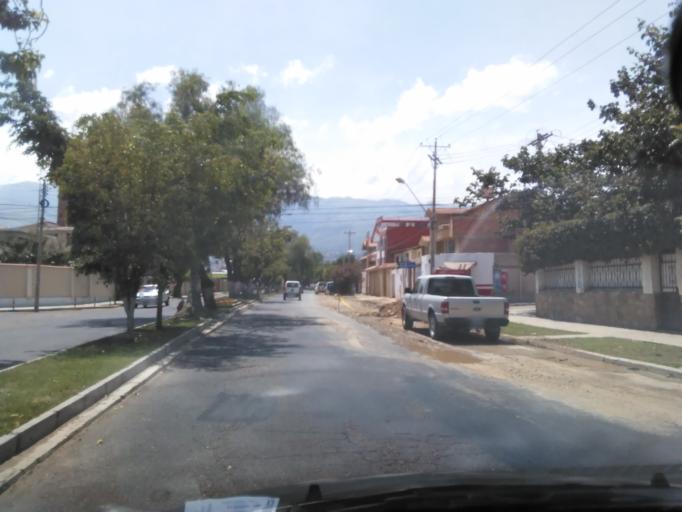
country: BO
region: Cochabamba
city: Cochabamba
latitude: -17.3855
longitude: -66.1652
